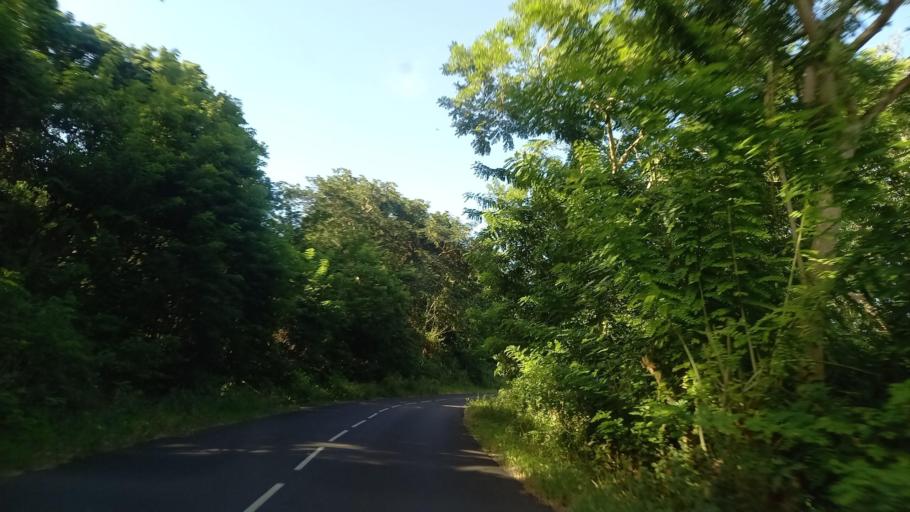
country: YT
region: Kani-Keli
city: Kani Keli
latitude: -12.9779
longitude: 45.1086
